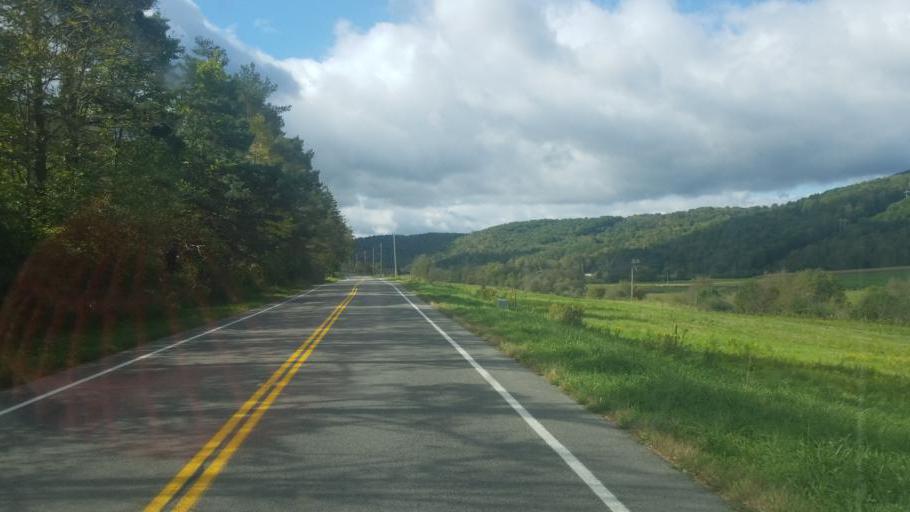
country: US
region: New York
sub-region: Cattaraugus County
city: Weston Mills
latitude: 42.1323
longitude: -78.3385
